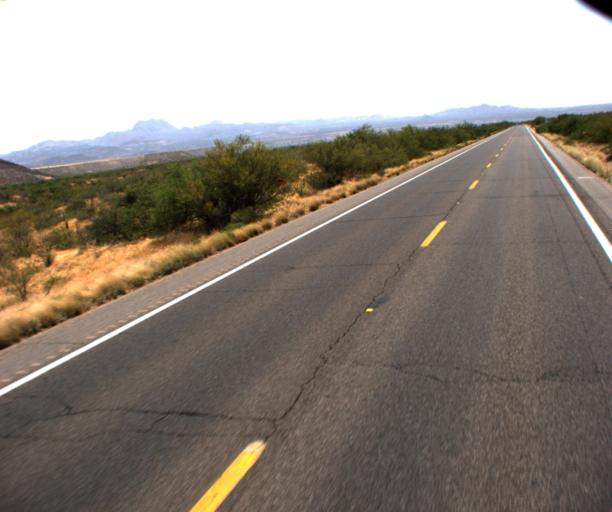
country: US
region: Arizona
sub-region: Gila County
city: Peridot
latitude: 33.3129
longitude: -110.5126
